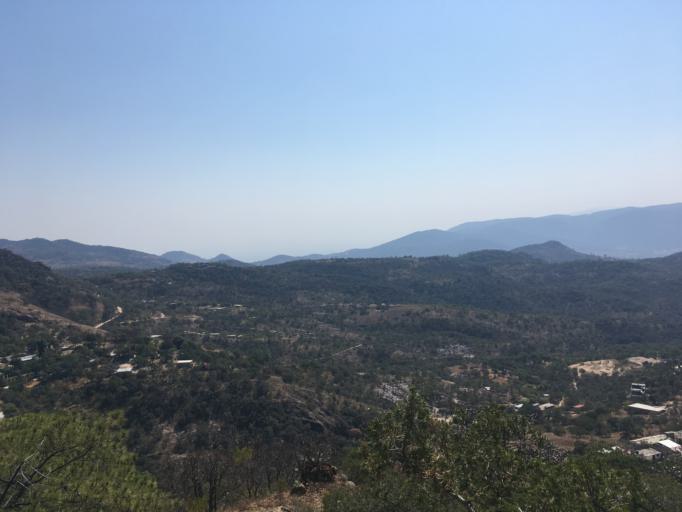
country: MX
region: Guerrero
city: Taxco de Alarcon
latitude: 18.5809
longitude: -99.6029
